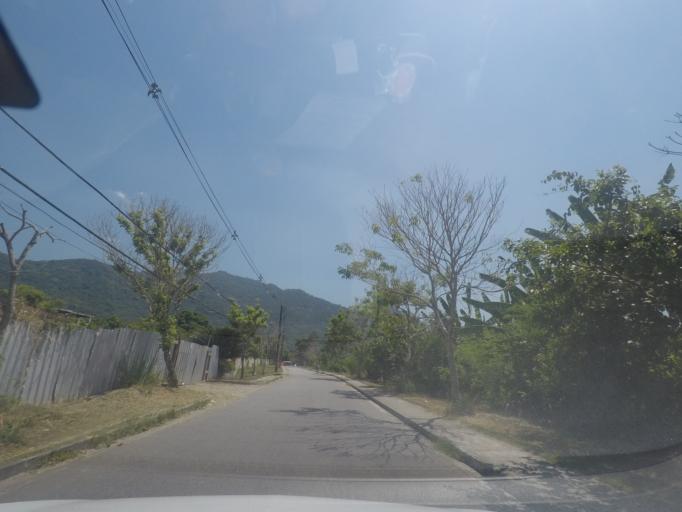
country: BR
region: Rio de Janeiro
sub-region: Nilopolis
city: Nilopolis
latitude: -22.9870
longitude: -43.4606
